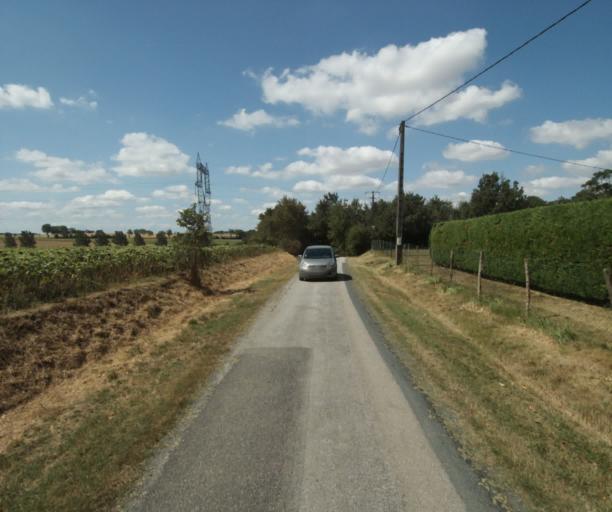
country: FR
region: Midi-Pyrenees
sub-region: Departement de la Haute-Garonne
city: Auriac-sur-Vendinelle
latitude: 43.4728
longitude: 1.8052
